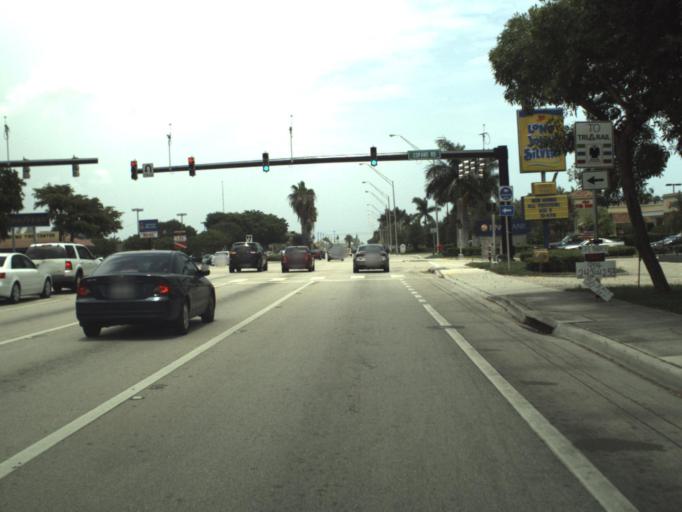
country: US
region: Florida
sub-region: Broward County
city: Lighthouse Point
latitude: 26.2582
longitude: -80.0997
